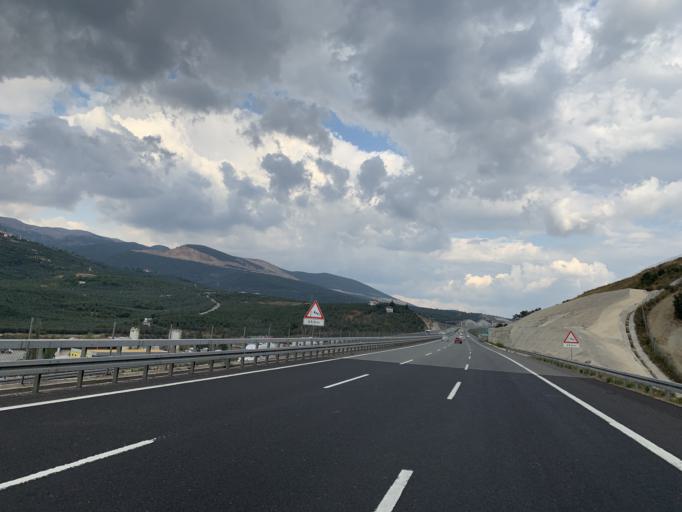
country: TR
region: Bursa
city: Umurbey
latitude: 40.4224
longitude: 29.1891
